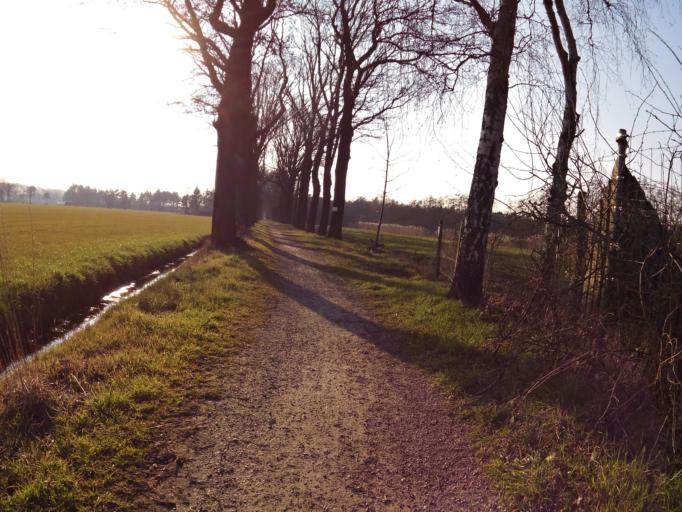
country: NL
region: North Brabant
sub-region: Gemeente Maasdonk
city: Geffen
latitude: 51.7043
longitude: 5.4237
